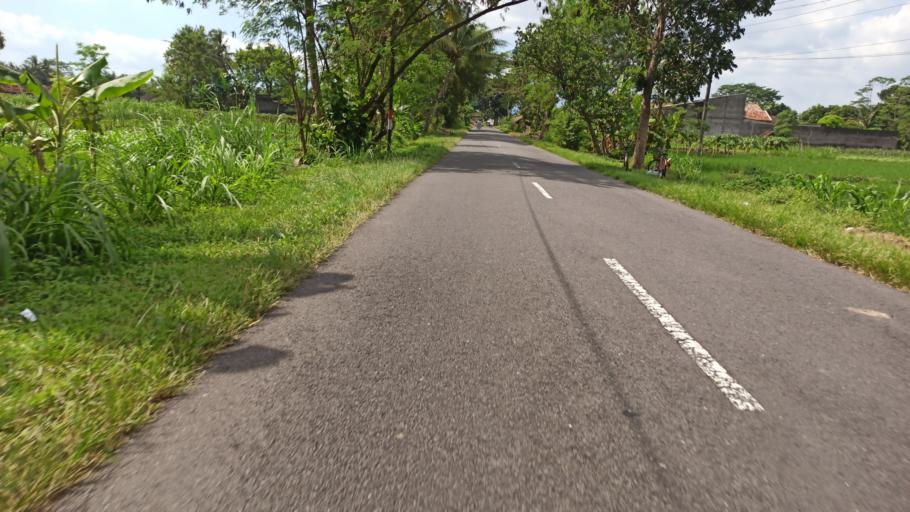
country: ID
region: Daerah Istimewa Yogyakarta
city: Sleman
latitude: -7.6891
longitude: 110.2971
